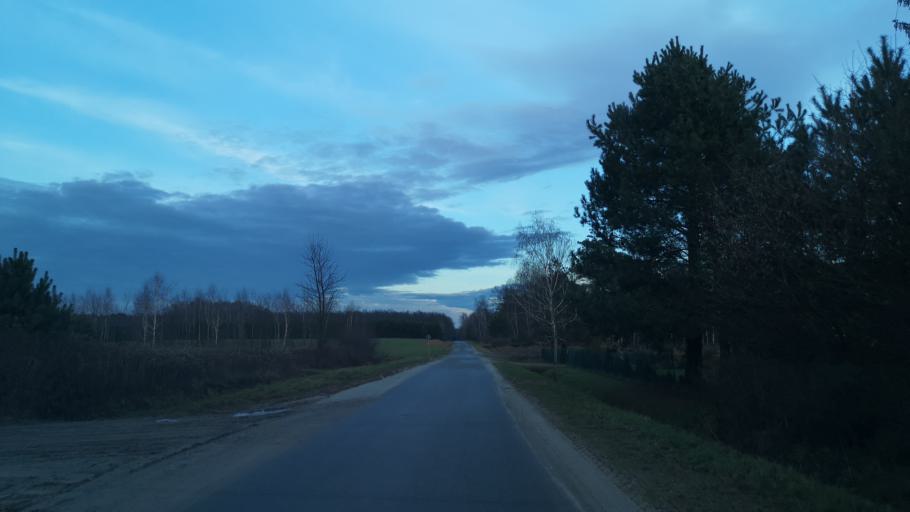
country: PL
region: Subcarpathian Voivodeship
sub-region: Powiat przeworski
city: Adamowka
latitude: 50.2544
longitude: 22.6384
